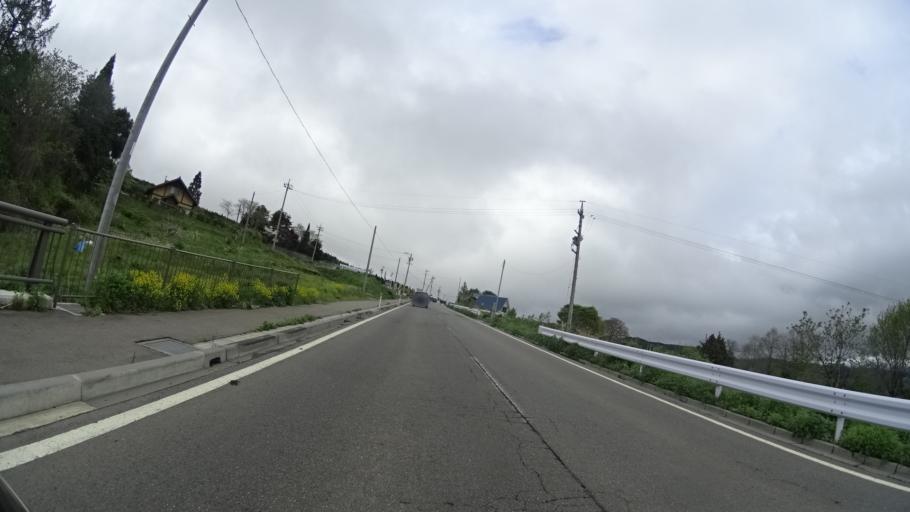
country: JP
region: Nagano
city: Nagano-shi
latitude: 36.7407
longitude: 138.2057
